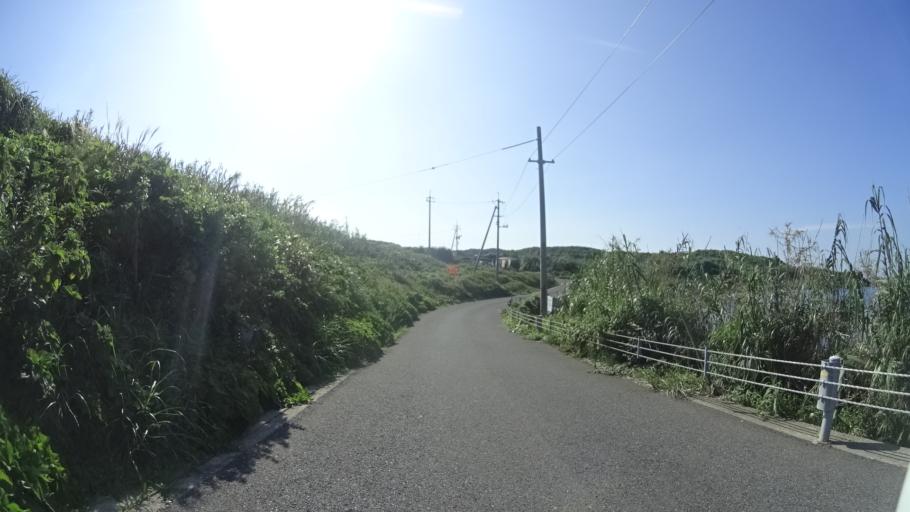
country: JP
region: Yamaguchi
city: Nagato
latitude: 34.3506
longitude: 130.8395
